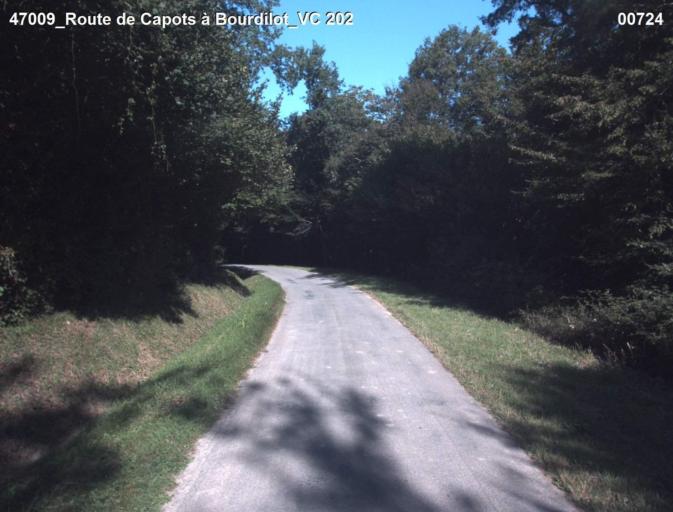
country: FR
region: Aquitaine
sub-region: Departement du Lot-et-Garonne
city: Mezin
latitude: 44.0999
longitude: 0.2996
